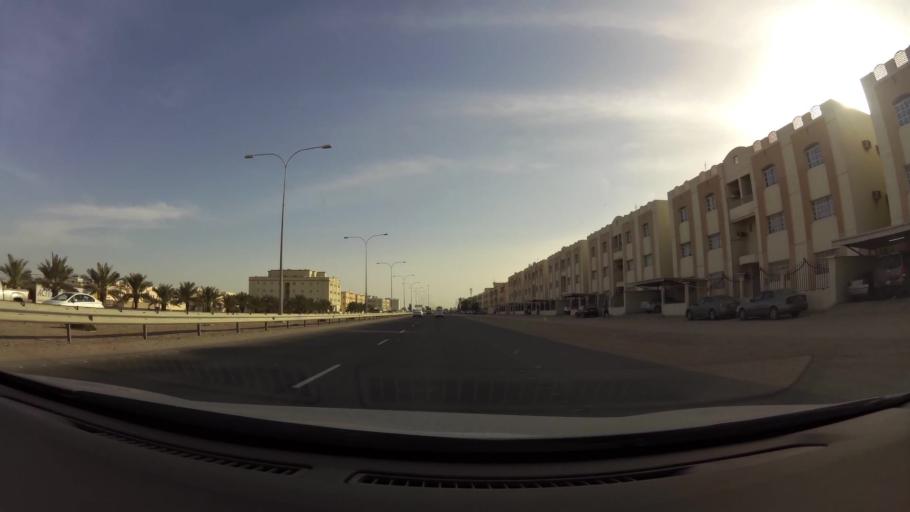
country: QA
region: Al Wakrah
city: Al Wakrah
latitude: 25.1547
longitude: 51.6042
